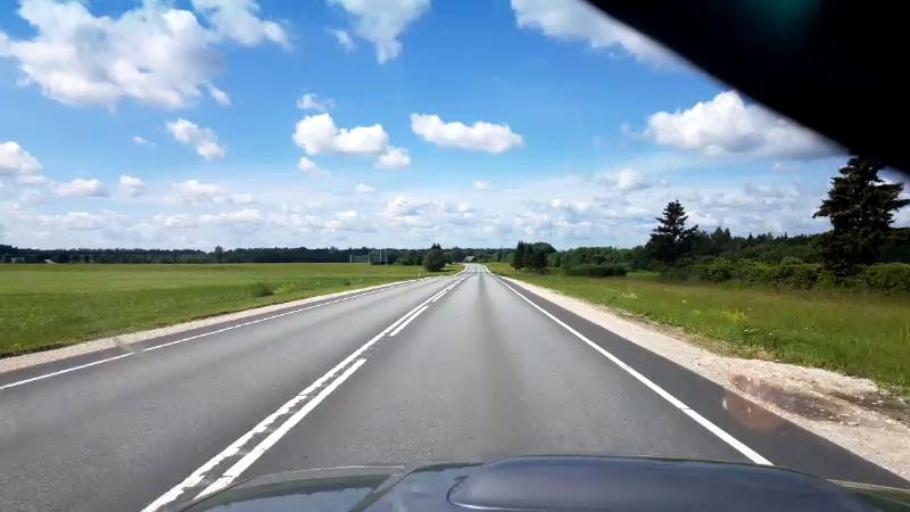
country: EE
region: Laeaene-Virumaa
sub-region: Tapa vald
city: Tapa
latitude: 59.2633
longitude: 26.0161
